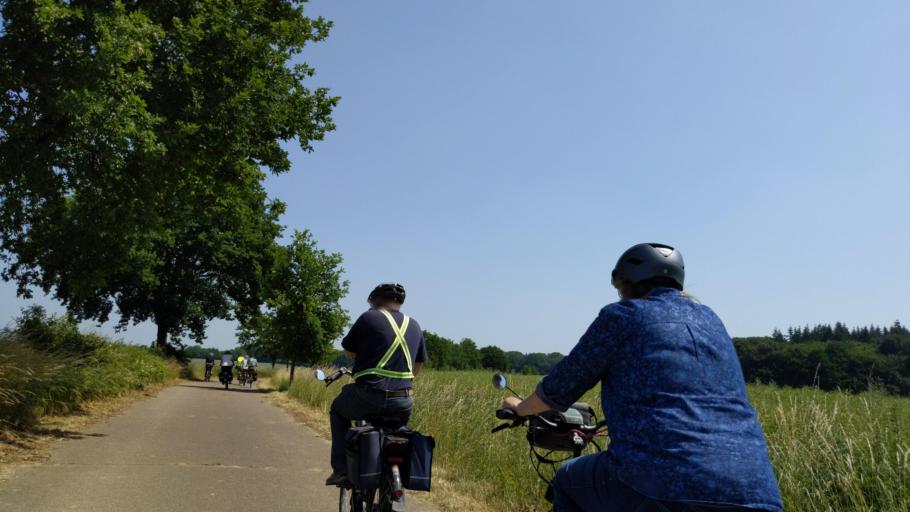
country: DE
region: Schleswig-Holstein
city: Behlendorf
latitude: 53.6911
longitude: 10.6774
